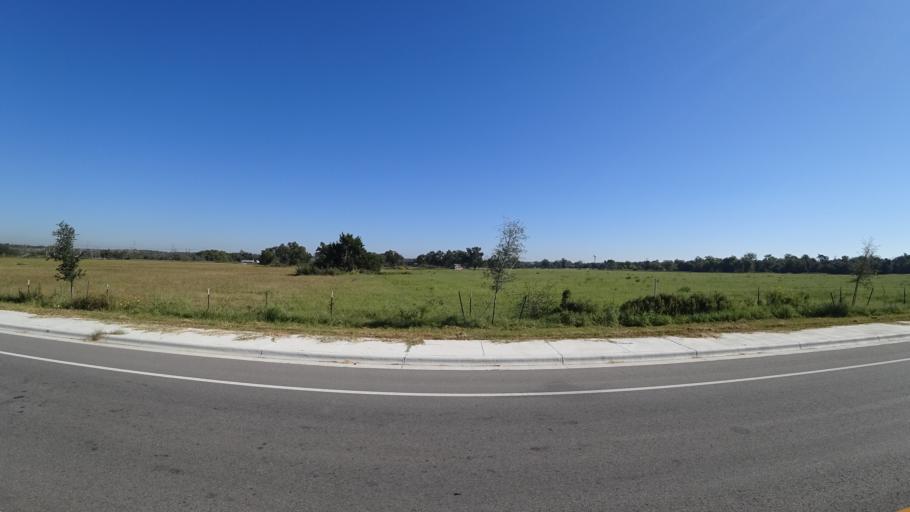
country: US
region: Texas
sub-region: Travis County
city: Hornsby Bend
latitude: 30.2477
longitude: -97.5950
